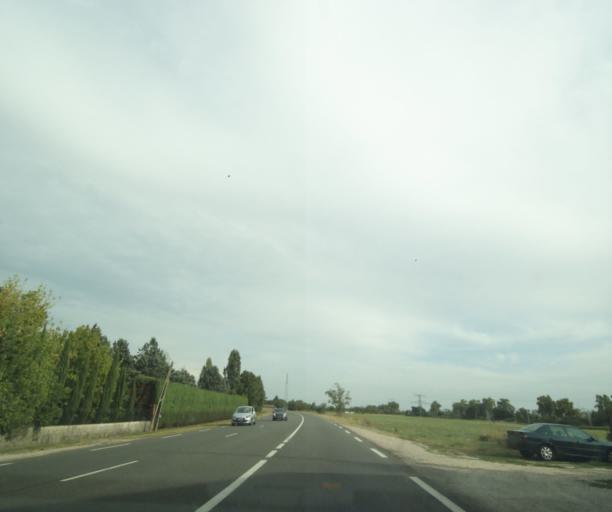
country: FR
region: Midi-Pyrenees
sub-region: Departement de la Haute-Garonne
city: Castelnau-d'Estretefonds
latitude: 43.7941
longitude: 1.3365
